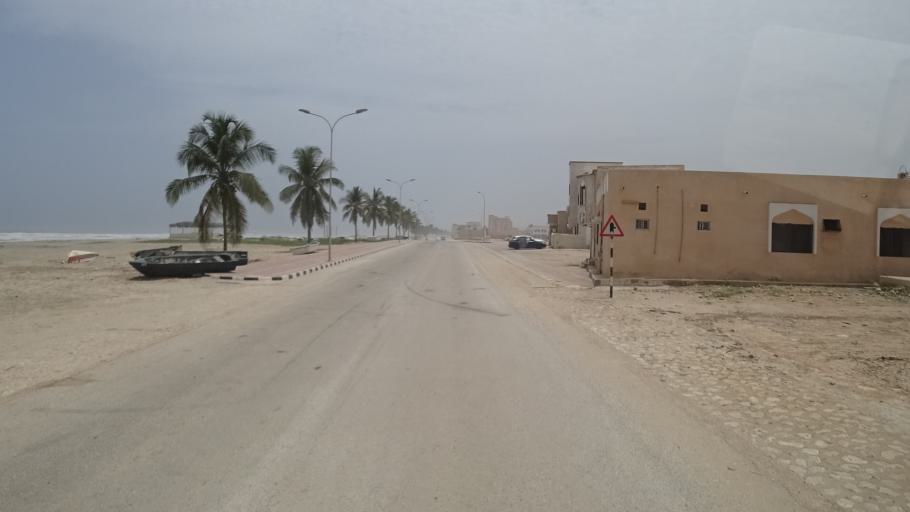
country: OM
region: Zufar
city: Salalah
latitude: 17.0348
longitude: 54.4051
